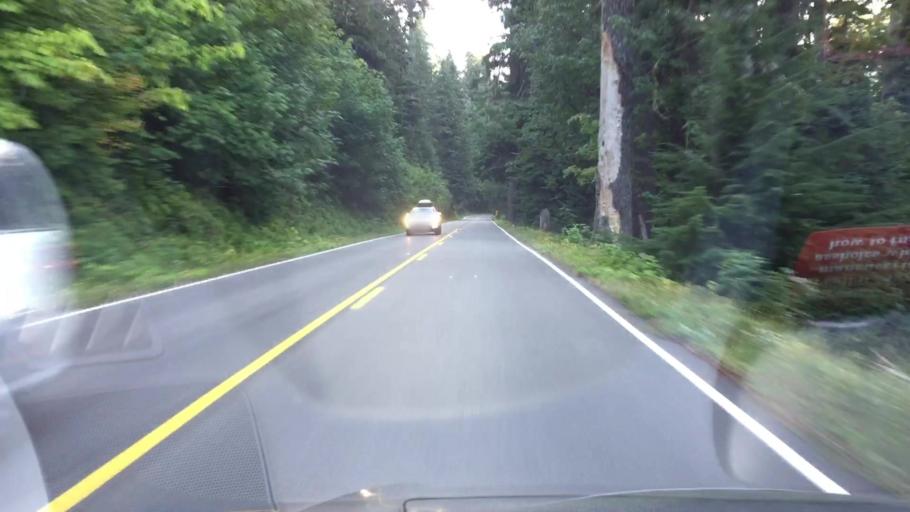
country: US
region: Washington
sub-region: Pierce County
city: Buckley
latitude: 46.7441
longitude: -121.5757
